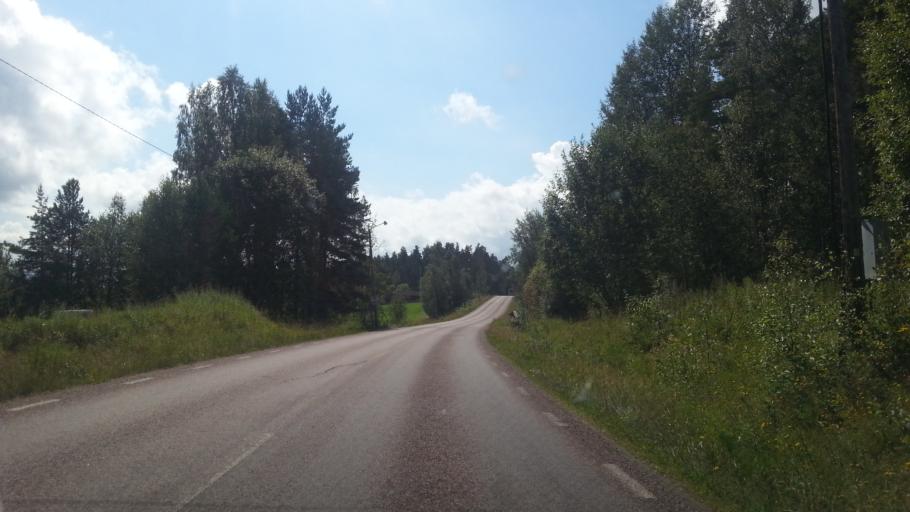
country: SE
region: Dalarna
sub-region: Faluns Kommun
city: Falun
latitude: 60.6211
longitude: 15.7669
